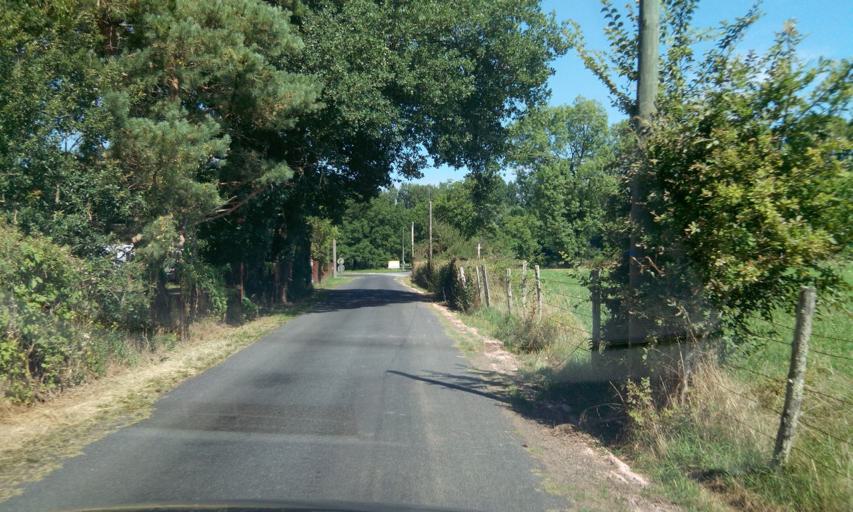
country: FR
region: Midi-Pyrenees
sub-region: Departement du Lot
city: Vayrac
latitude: 44.9388
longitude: 1.6687
